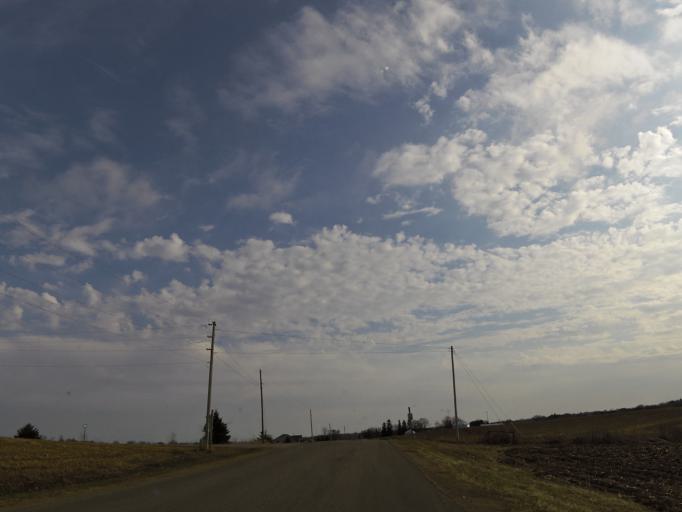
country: US
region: Wisconsin
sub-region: Pierce County
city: Ellsworth
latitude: 44.7472
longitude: -92.4669
